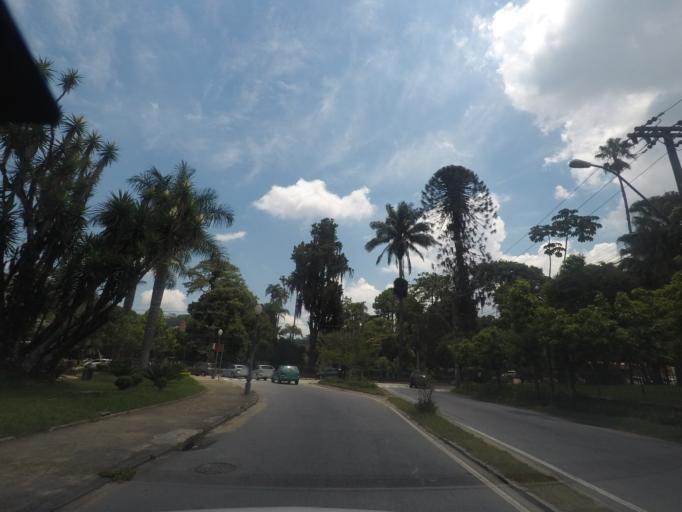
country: BR
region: Rio de Janeiro
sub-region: Petropolis
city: Petropolis
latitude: -22.5056
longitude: -43.1798
